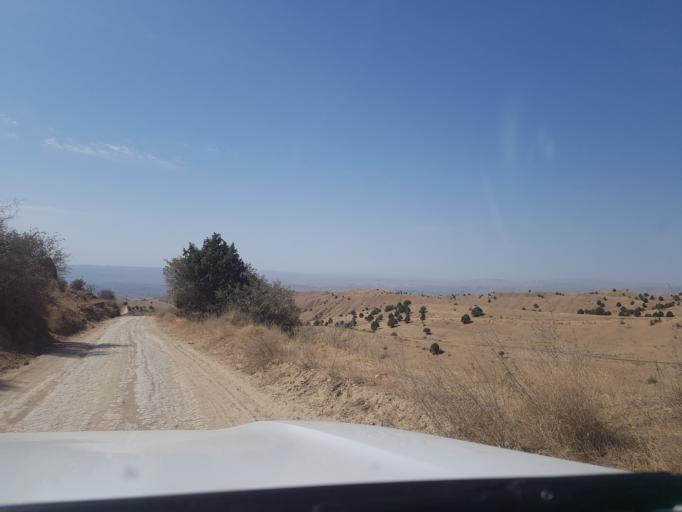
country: TM
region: Ahal
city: Baharly
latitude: 38.3055
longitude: 56.9461
